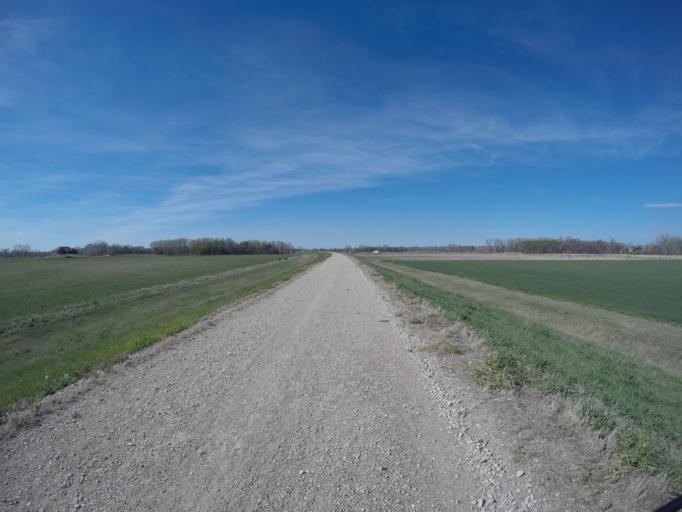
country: US
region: Kansas
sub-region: Saline County
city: Salina
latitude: 38.7911
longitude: -97.5765
